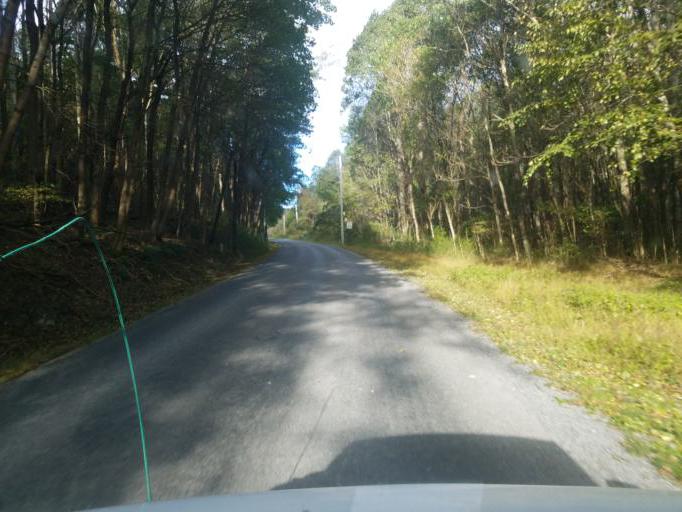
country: US
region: Pennsylvania
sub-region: Franklin County
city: Fayetteville
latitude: 39.8963
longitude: -77.4108
